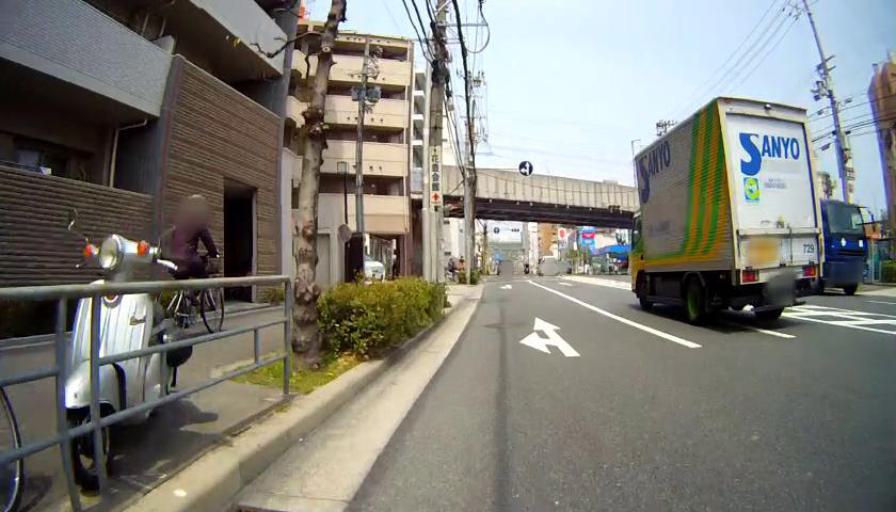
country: JP
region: Osaka
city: Suita
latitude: 34.7455
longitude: 135.5269
